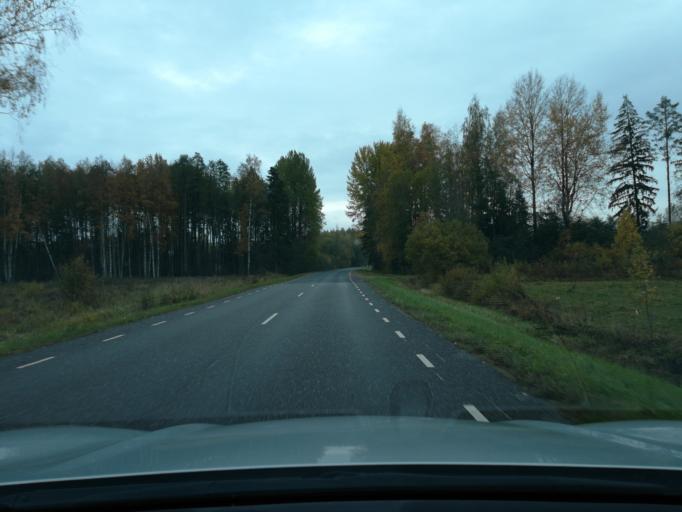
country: EE
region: Ida-Virumaa
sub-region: Johvi vald
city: Johvi
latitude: 59.0496
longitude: 27.3956
